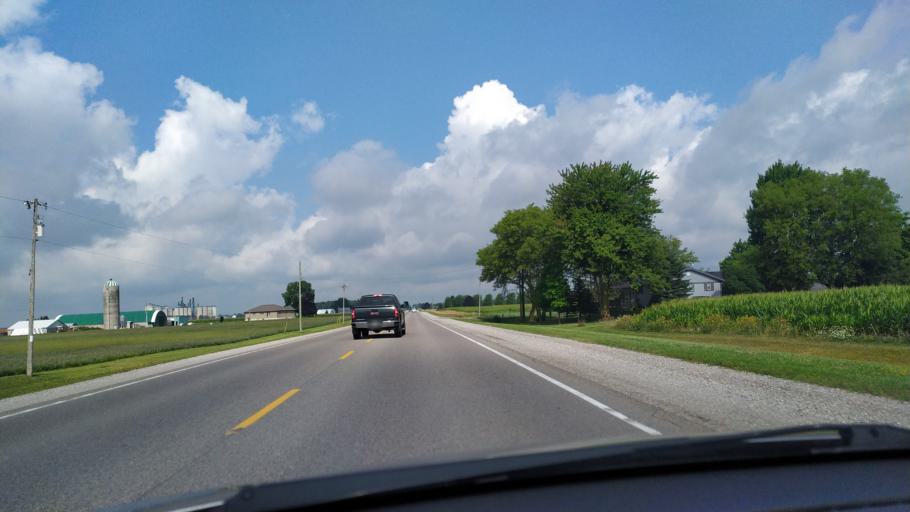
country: CA
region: Ontario
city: Huron East
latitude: 43.4529
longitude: -81.1633
